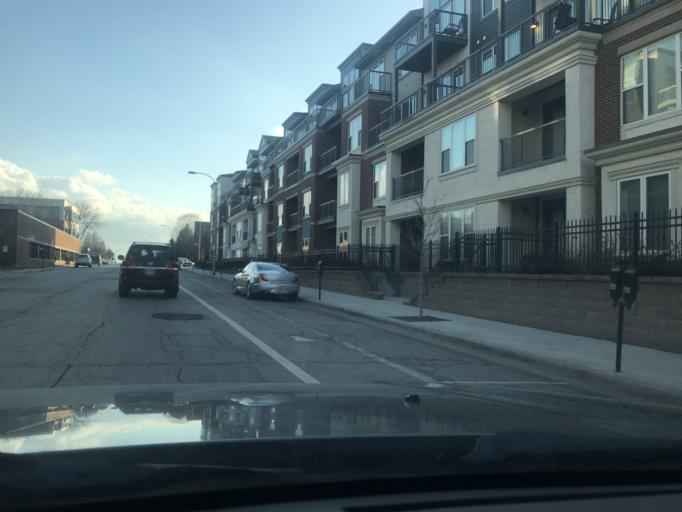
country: US
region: Missouri
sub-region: Jackson County
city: Kansas City
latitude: 39.0996
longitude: -94.5912
